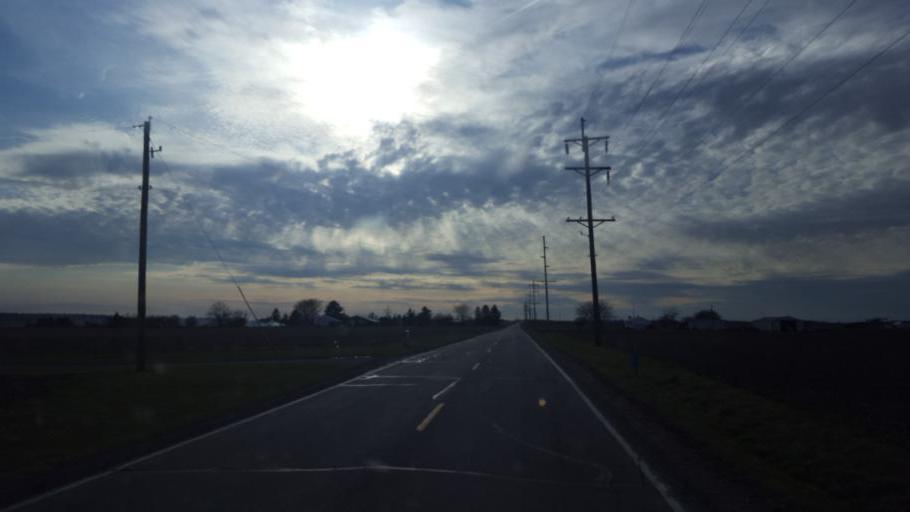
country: US
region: Ohio
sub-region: Crawford County
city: Bucyrus
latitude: 40.7839
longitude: -82.8868
